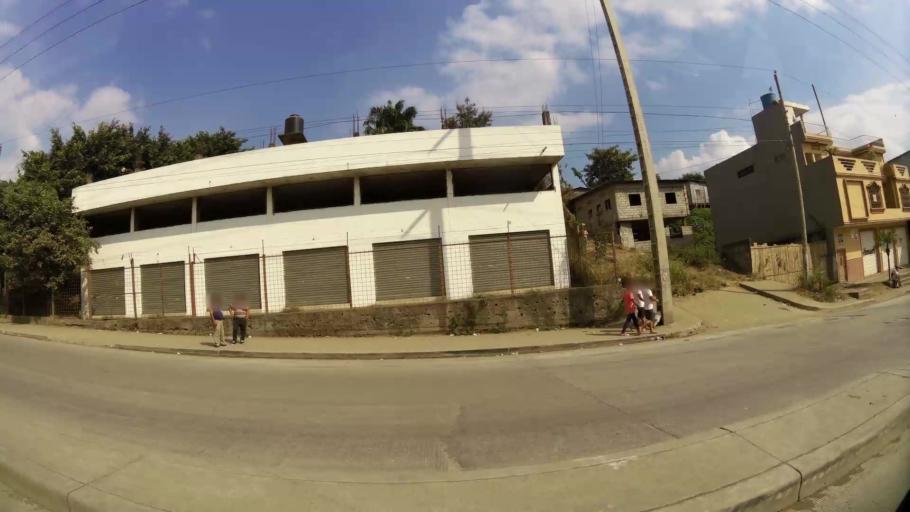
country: EC
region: Guayas
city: Santa Lucia
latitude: -2.1205
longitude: -79.9712
